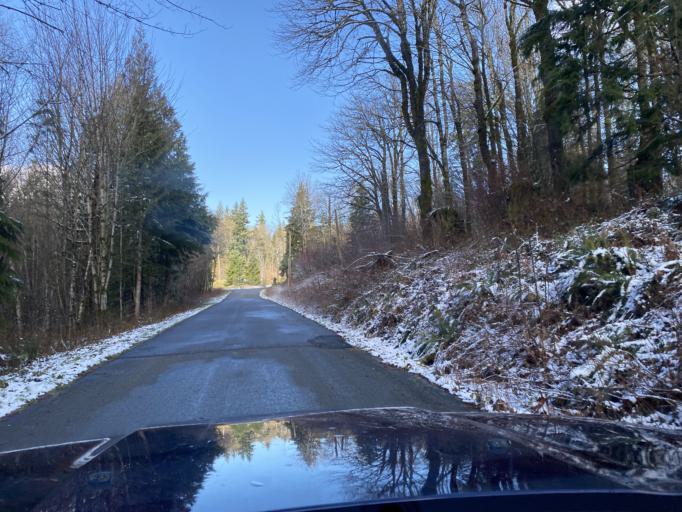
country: US
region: Washington
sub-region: King County
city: Snoqualmie
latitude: 47.5081
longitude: -121.8737
